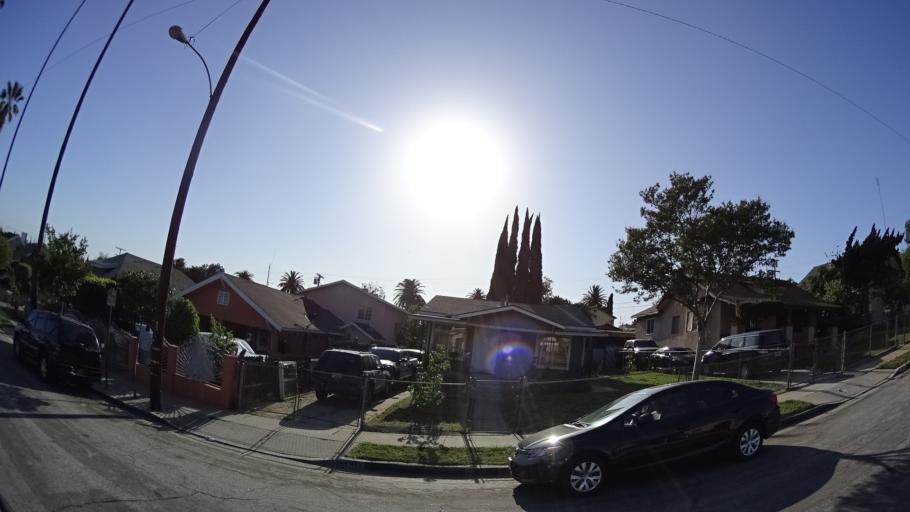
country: US
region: California
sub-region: Los Angeles County
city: Boyle Heights
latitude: 34.0420
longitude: -118.1904
